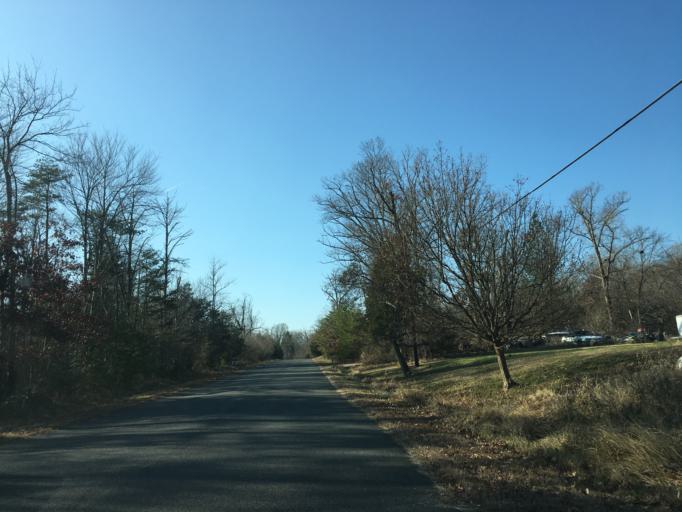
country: US
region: Virginia
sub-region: Fairfax County
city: Fairfax Station
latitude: 38.8249
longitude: -77.3680
